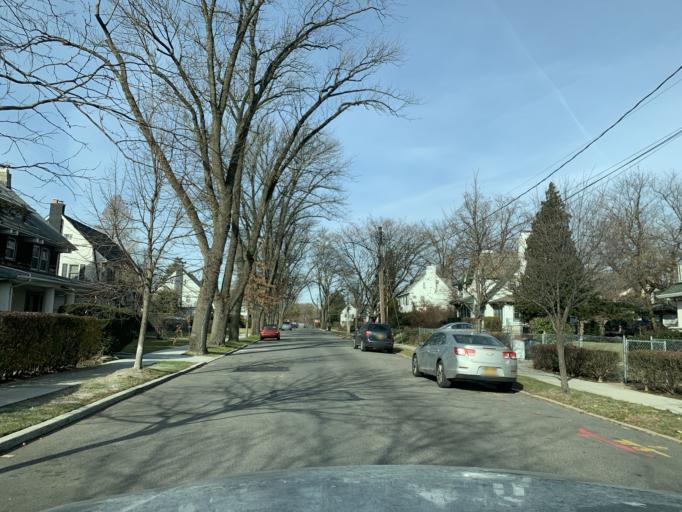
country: US
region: New York
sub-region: Queens County
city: Jamaica
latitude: 40.6928
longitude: -73.7684
